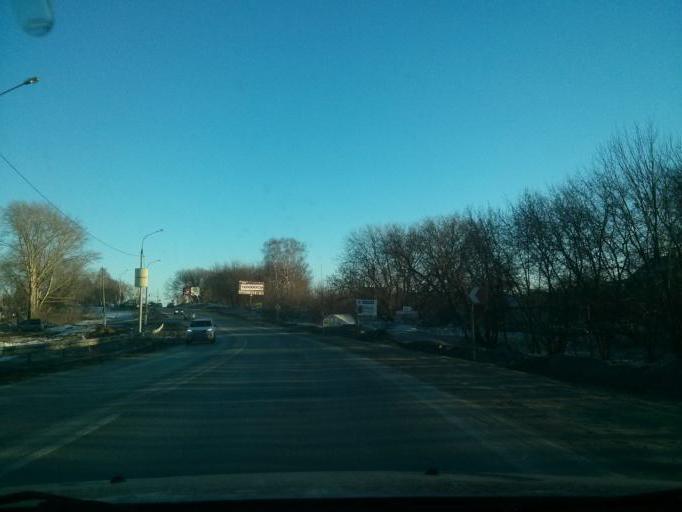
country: RU
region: Nizjnij Novgorod
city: Afonino
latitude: 56.2742
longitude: 44.0842
